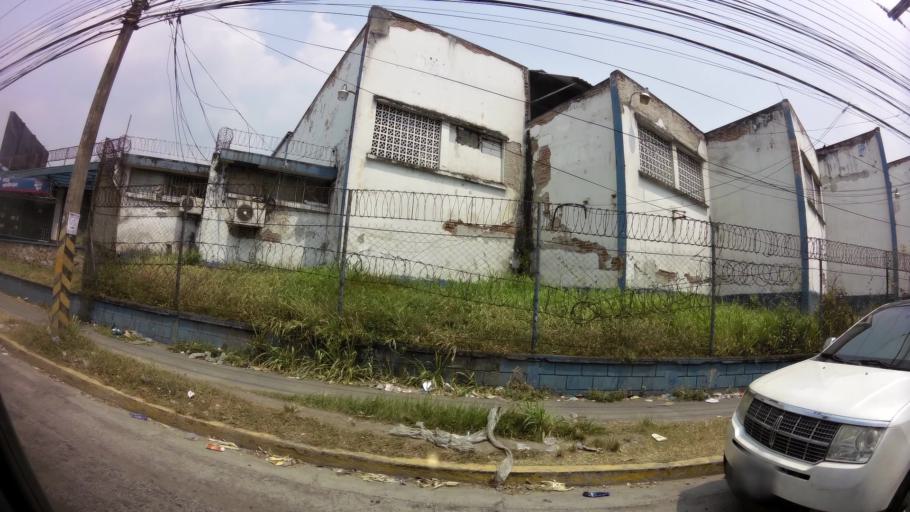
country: HN
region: Cortes
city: San Pedro Sula
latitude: 15.4849
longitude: -88.0300
